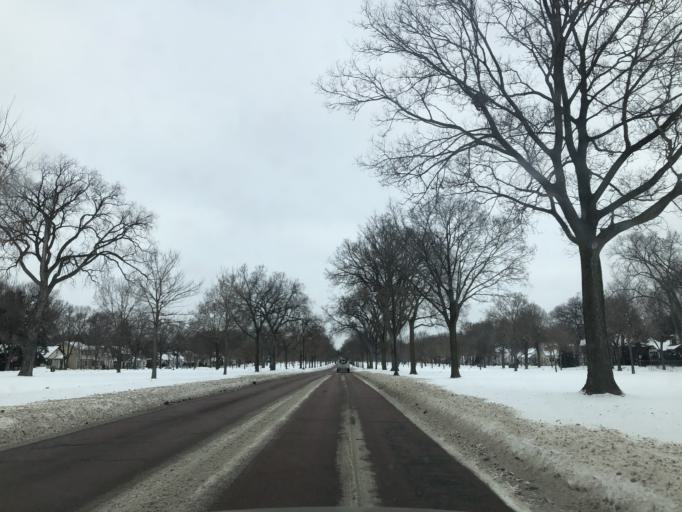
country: US
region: Minnesota
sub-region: Hennepin County
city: Robbinsdale
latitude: 45.0268
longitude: -93.3192
